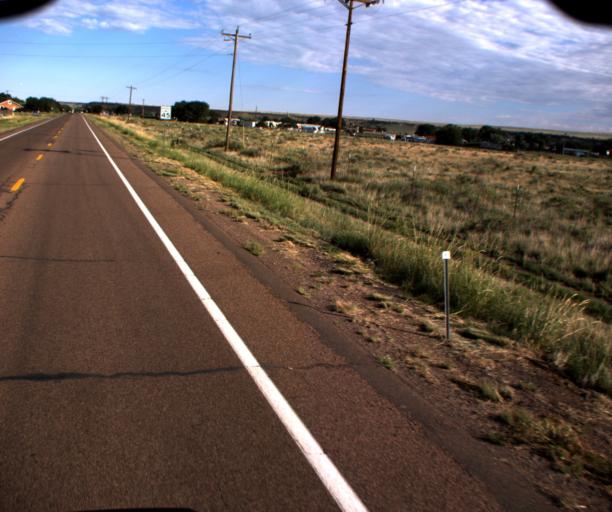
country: US
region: Arizona
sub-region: Apache County
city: Springerville
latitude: 34.1231
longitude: -109.2616
